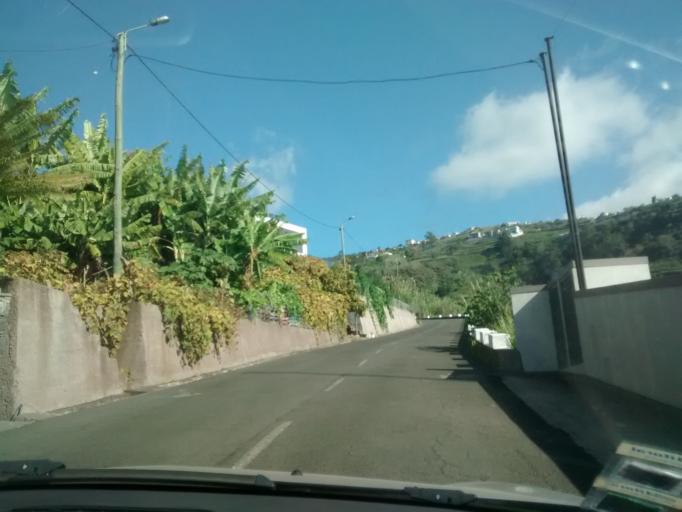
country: PT
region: Madeira
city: Calheta
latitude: 32.7207
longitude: -17.1674
